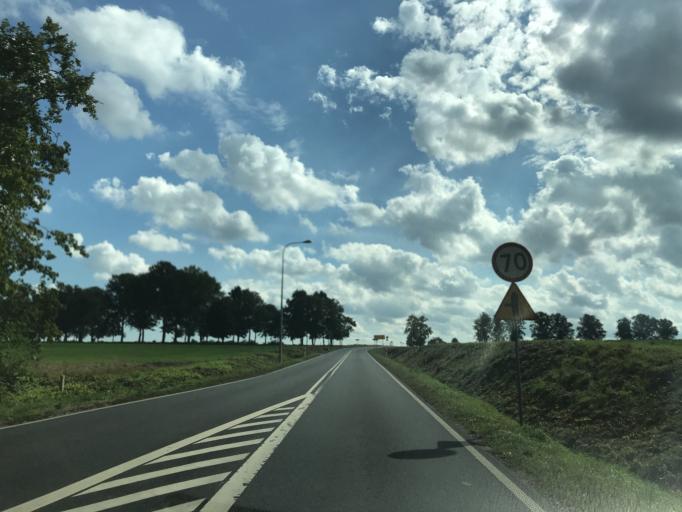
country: PL
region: Warmian-Masurian Voivodeship
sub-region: Powiat ilawski
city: Lubawa
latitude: 53.4221
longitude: 19.7819
